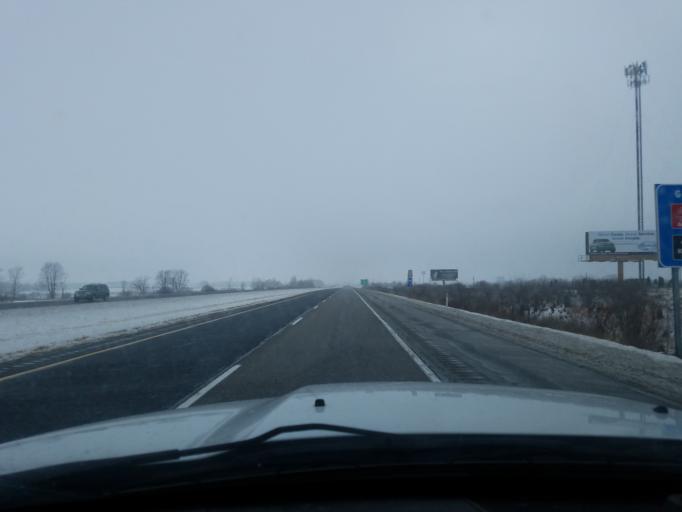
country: US
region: Indiana
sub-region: Fulton County
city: Rochester
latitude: 41.0429
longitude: -86.2060
